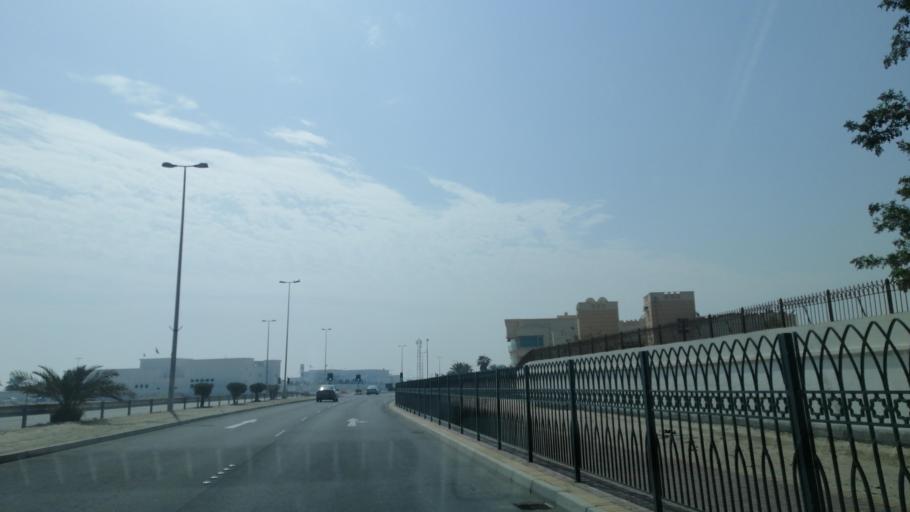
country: BH
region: Muharraq
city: Al Hadd
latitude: 26.2511
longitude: 50.6570
